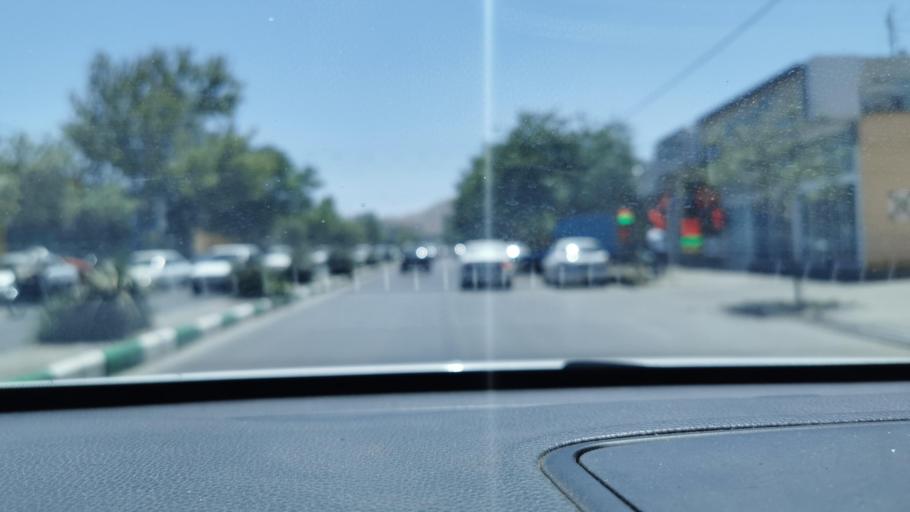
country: IR
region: Razavi Khorasan
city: Mashhad
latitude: 36.2618
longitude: 59.6039
